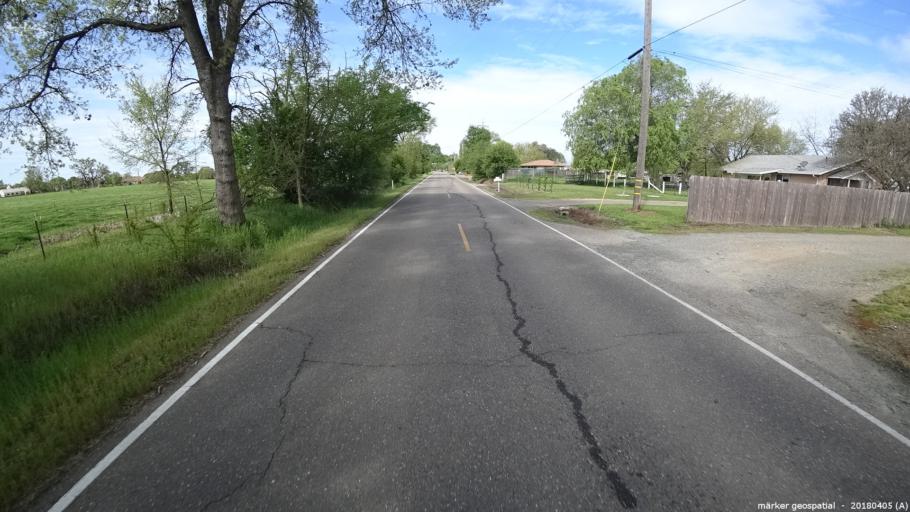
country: US
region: California
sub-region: Sacramento County
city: Galt
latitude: 38.2619
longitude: -121.3337
